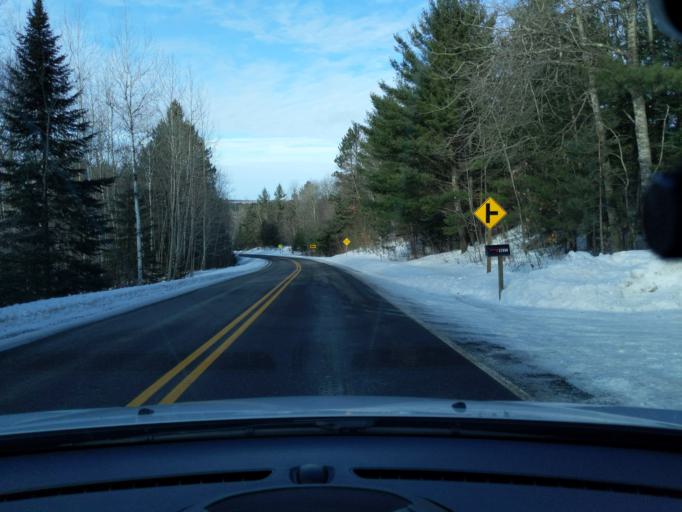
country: US
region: Wisconsin
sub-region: Sawyer County
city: Little Round Lake
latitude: 46.1194
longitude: -91.3422
